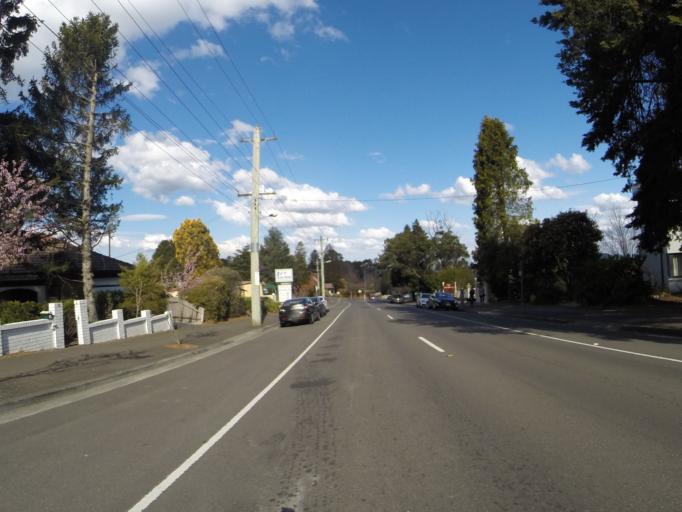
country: AU
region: New South Wales
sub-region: Blue Mountains Municipality
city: Katoomba
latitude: -33.7291
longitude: 150.3112
